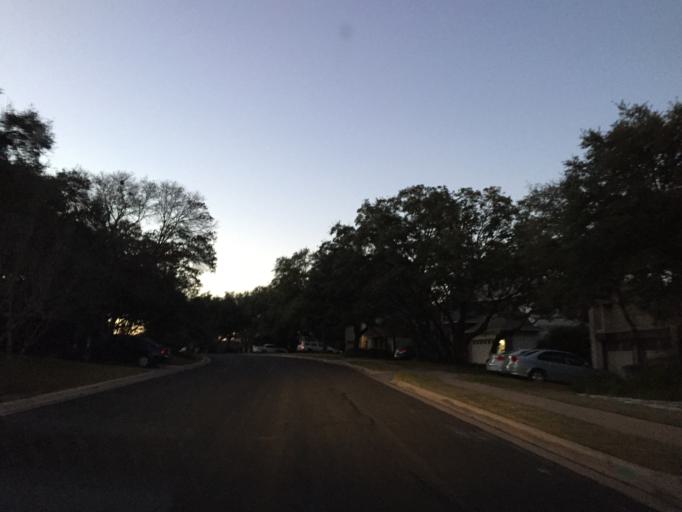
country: US
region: Texas
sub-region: Travis County
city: Wells Branch
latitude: 30.3999
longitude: -97.6933
